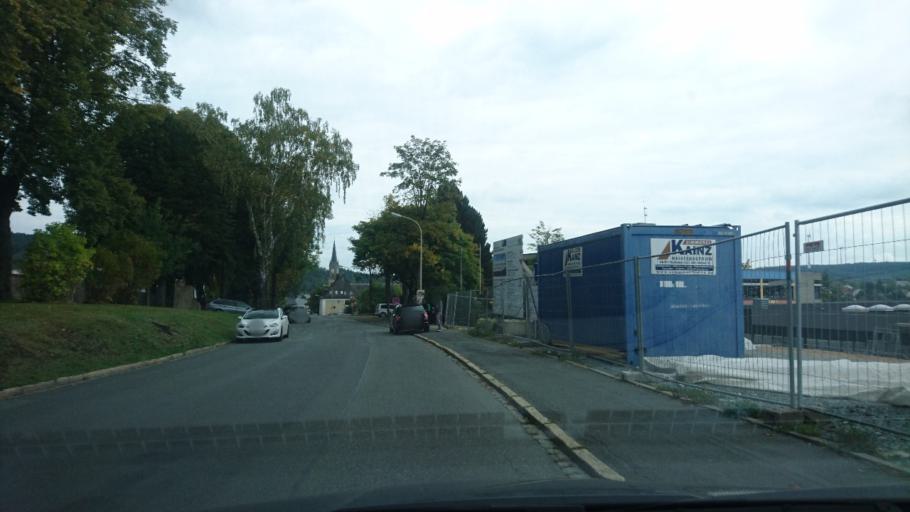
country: DE
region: Bavaria
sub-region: Upper Franconia
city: Naila
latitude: 50.3314
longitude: 11.7025
